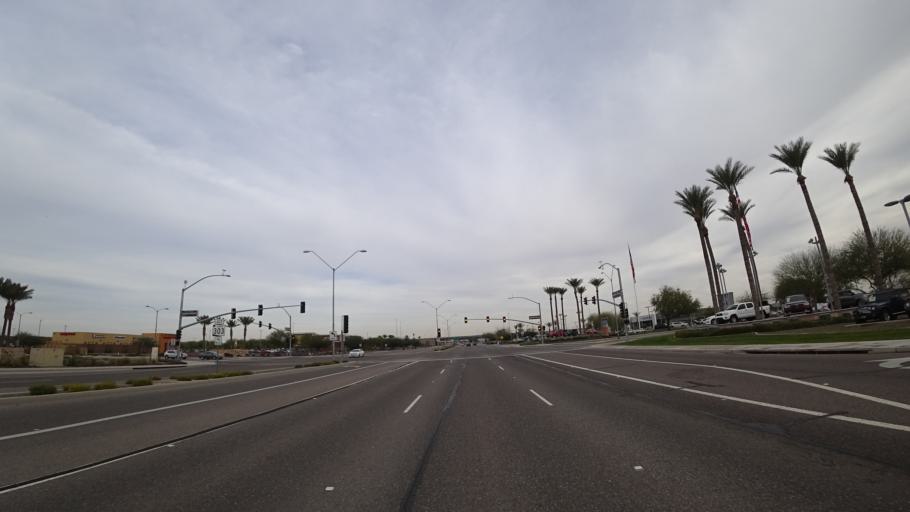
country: US
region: Arizona
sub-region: Maricopa County
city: Citrus Park
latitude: 33.6097
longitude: -112.4233
